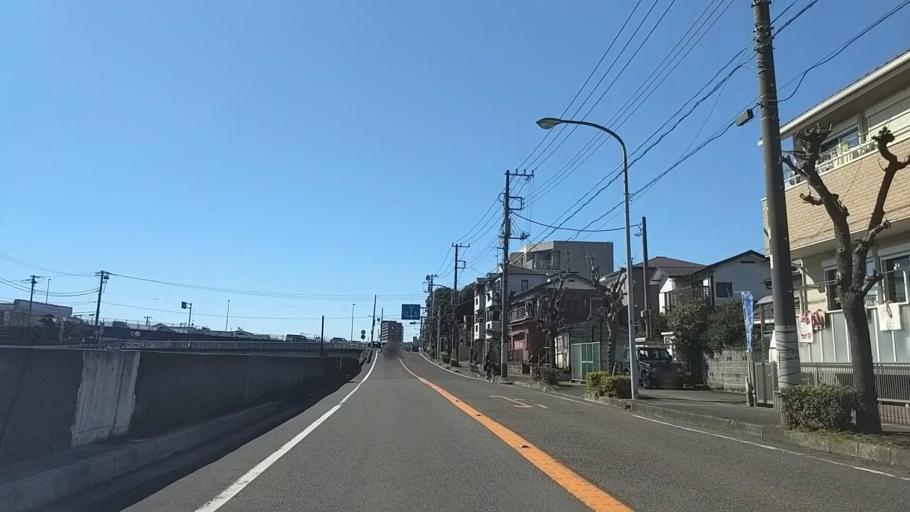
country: JP
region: Kanagawa
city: Kamakura
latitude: 35.3484
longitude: 139.5240
